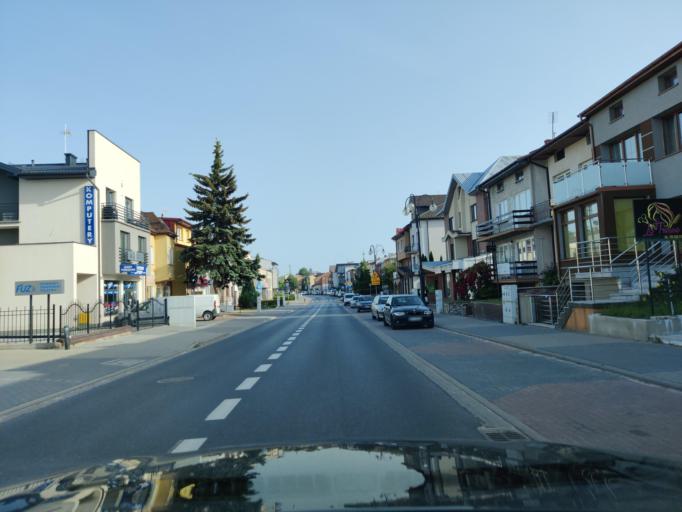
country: PL
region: Masovian Voivodeship
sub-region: Powiat wyszkowski
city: Wyszkow
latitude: 52.5975
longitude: 21.4565
